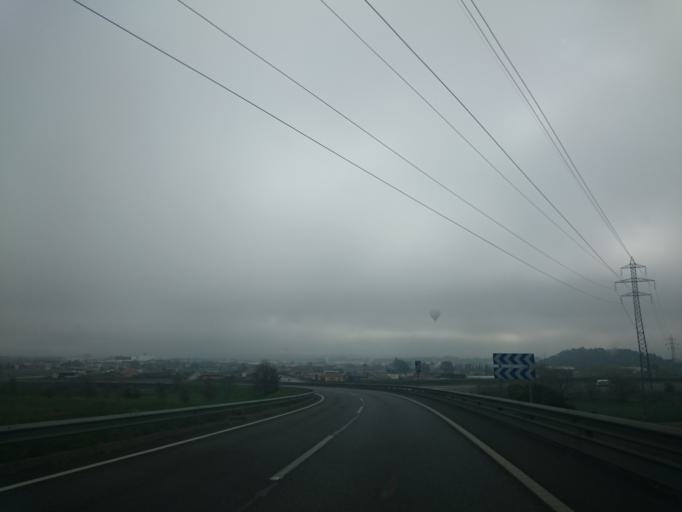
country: ES
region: Catalonia
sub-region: Provincia de Barcelona
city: Gurb
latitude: 41.9393
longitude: 2.2289
